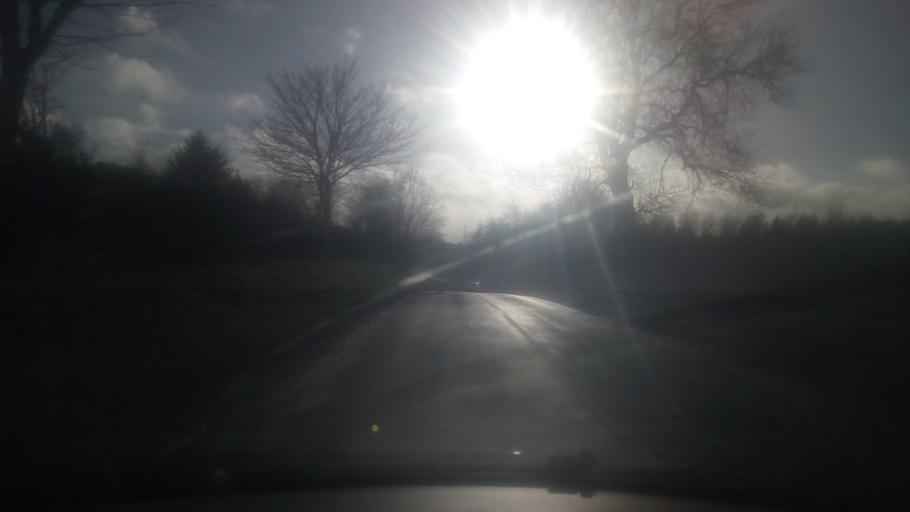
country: GB
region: Scotland
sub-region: The Scottish Borders
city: Coldstream
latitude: 55.7038
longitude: -2.3030
